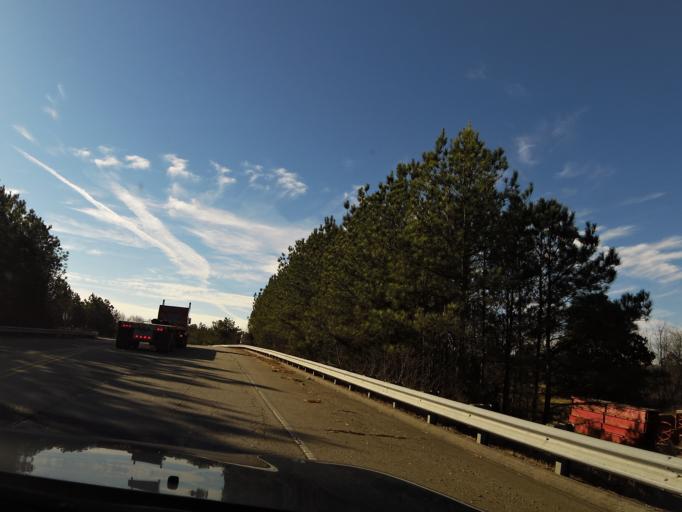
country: US
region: Virginia
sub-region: City of Petersburg
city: Petersburg
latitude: 37.1889
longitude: -77.4230
